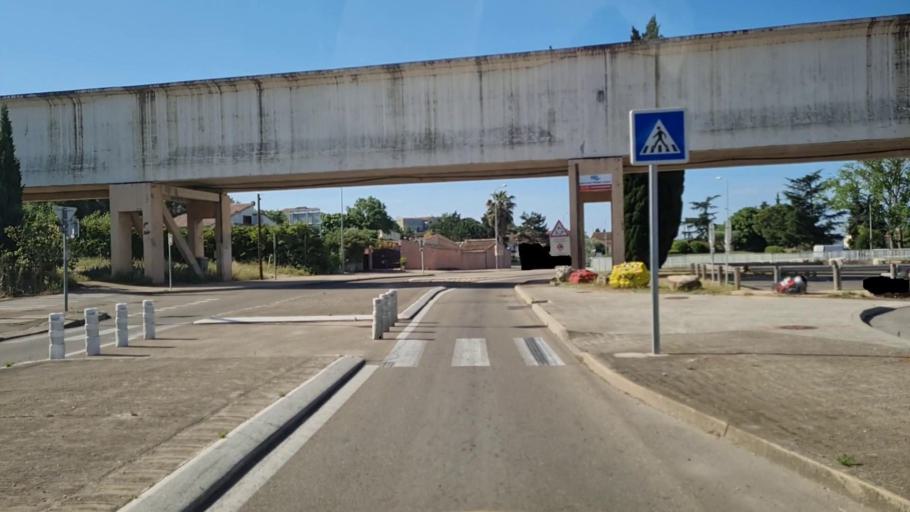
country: FR
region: Languedoc-Roussillon
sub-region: Departement du Gard
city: Saint-Gilles
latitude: 43.6833
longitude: 4.4300
